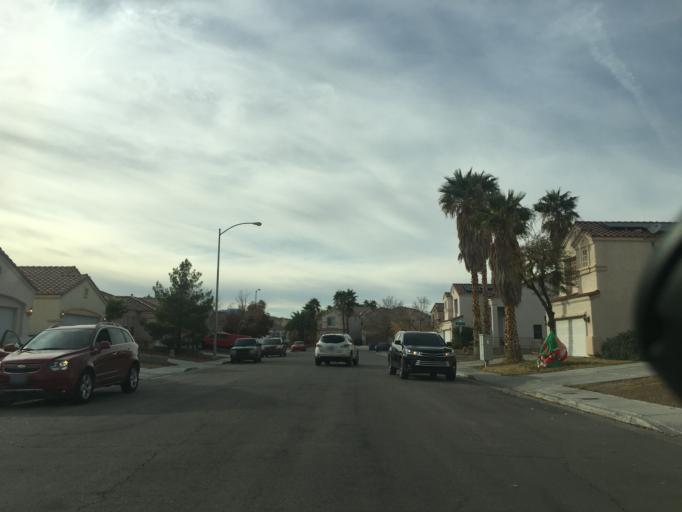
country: US
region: Nevada
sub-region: Clark County
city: Enterprise
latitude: 36.0168
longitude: -115.1673
